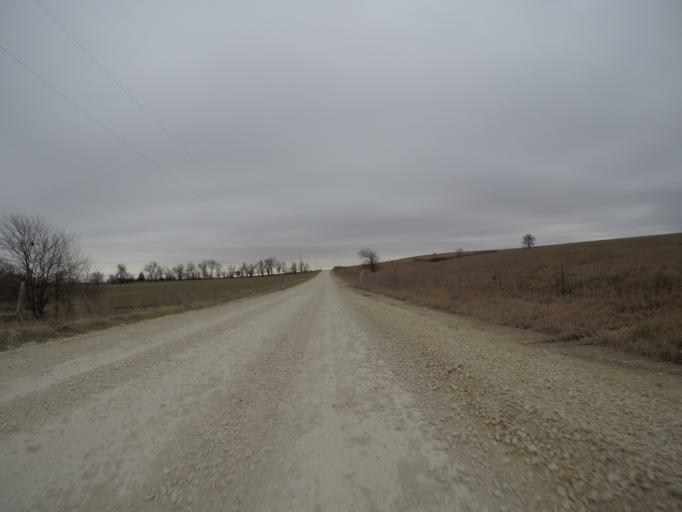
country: US
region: Kansas
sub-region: Wabaunsee County
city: Alma
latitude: 38.8498
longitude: -96.1133
